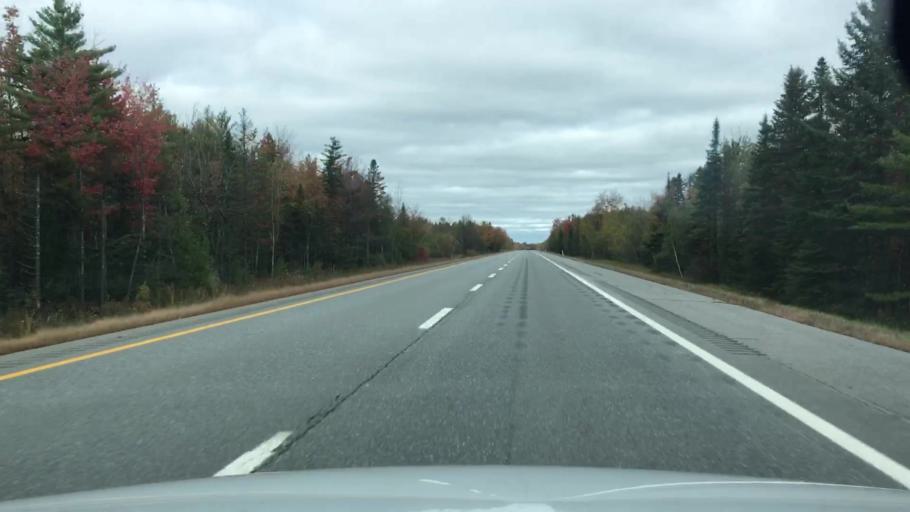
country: US
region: Maine
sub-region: Kennebec County
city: Clinton
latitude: 44.6756
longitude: -69.4827
